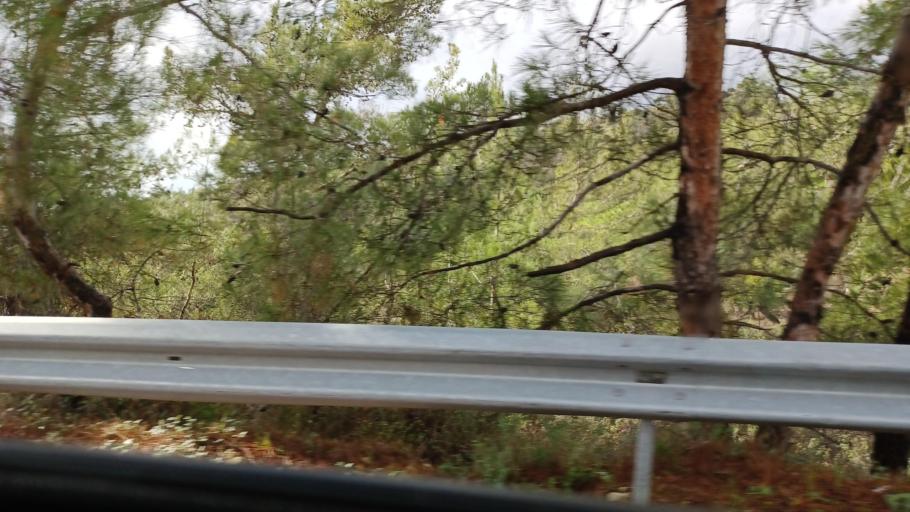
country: CY
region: Limassol
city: Sotira
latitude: 34.7103
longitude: 32.8659
